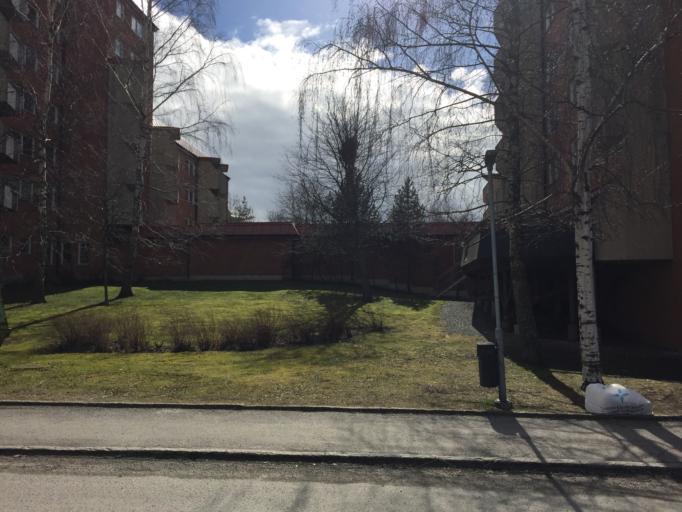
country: SE
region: Stockholm
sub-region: Stockholms Kommun
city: Bromma
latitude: 59.3041
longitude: 17.9727
